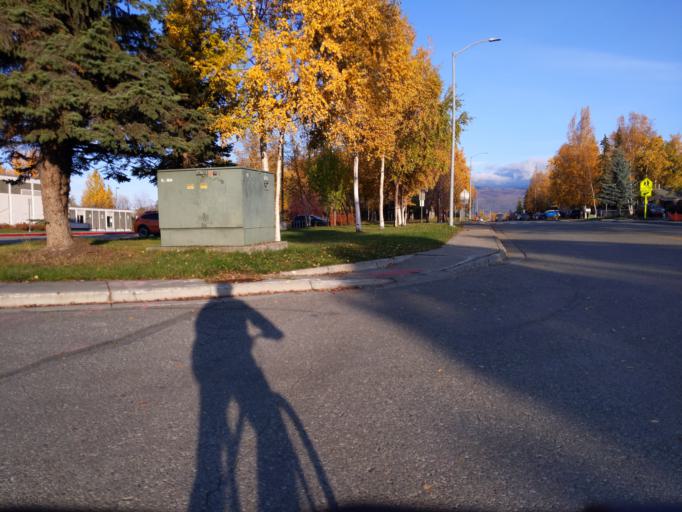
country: US
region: Alaska
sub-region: Anchorage Municipality
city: Anchorage
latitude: 61.1556
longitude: -149.8703
